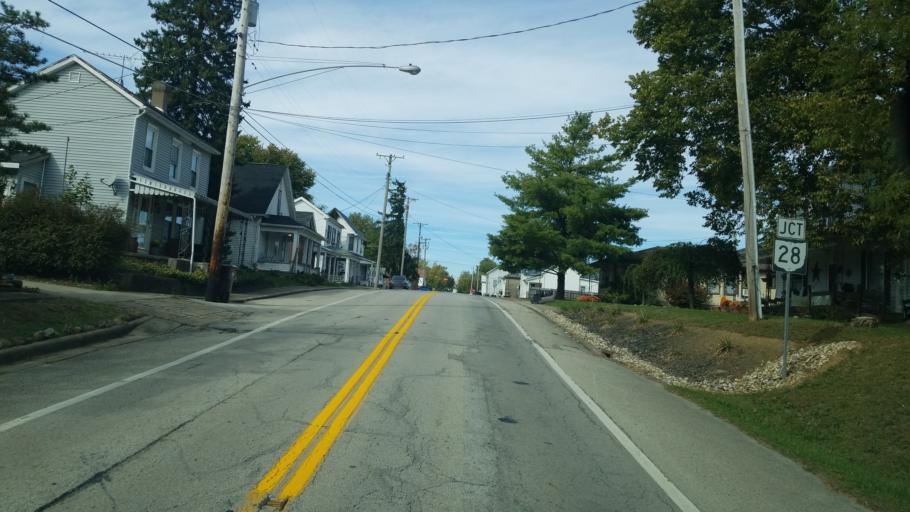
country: US
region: Ohio
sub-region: Highland County
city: Leesburg
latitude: 39.3428
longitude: -83.5979
